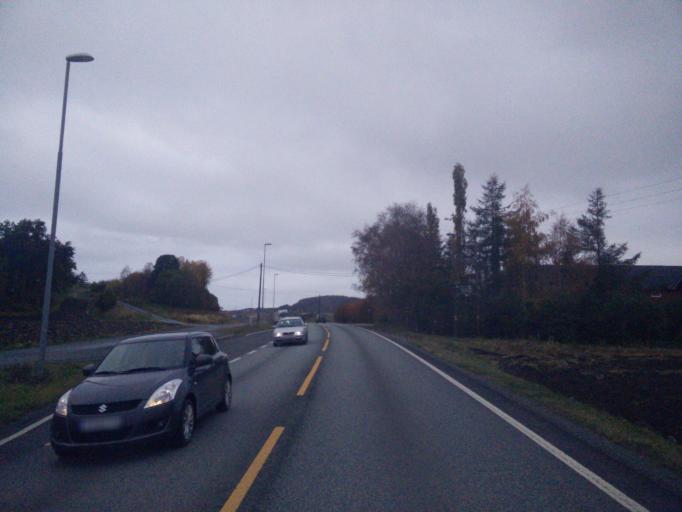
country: NO
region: Nord-Trondelag
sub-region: Stjordal
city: Stjordal
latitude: 63.4965
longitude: 10.8805
